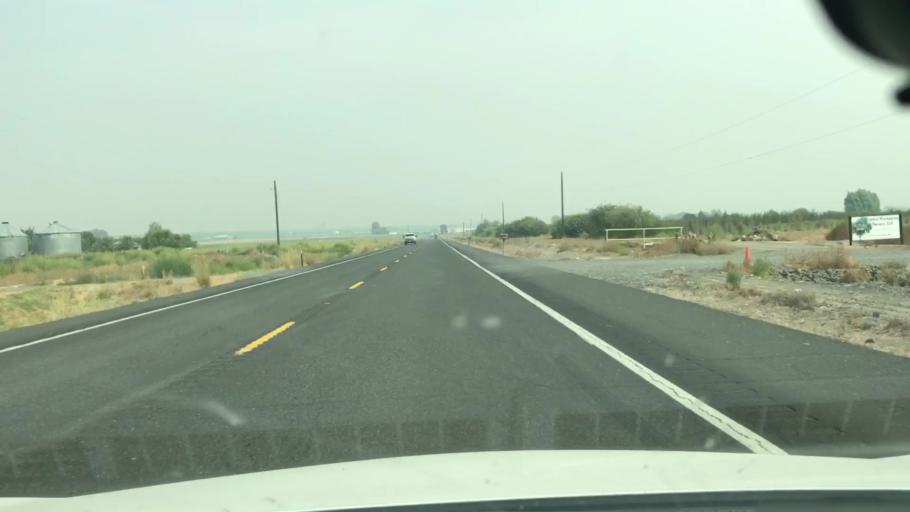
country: US
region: Washington
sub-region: Grant County
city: Quincy
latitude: 47.2417
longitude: -119.7364
